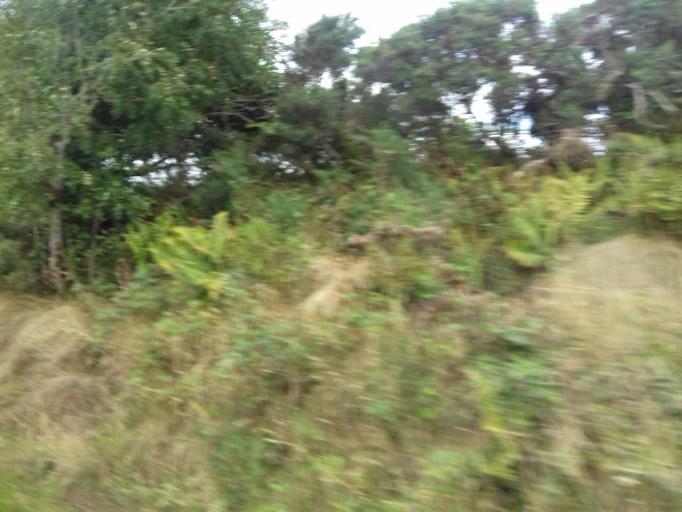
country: IE
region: Leinster
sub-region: Loch Garman
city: Bunclody
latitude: 52.6543
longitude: -6.7455
